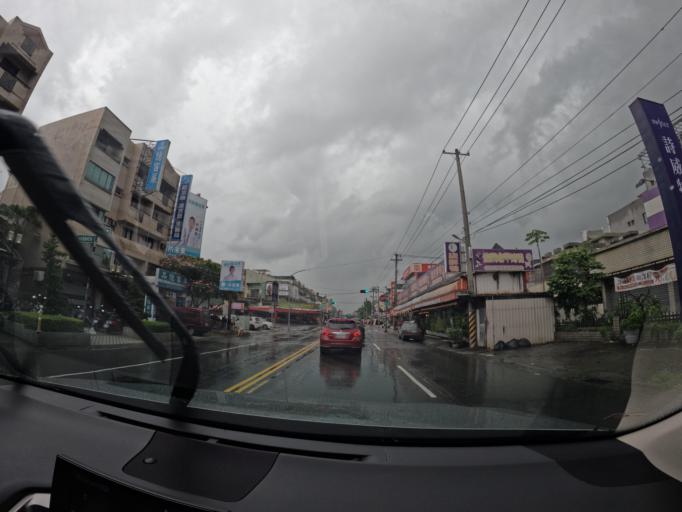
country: TW
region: Taiwan
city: Fengshan
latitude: 22.6553
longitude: 120.3364
